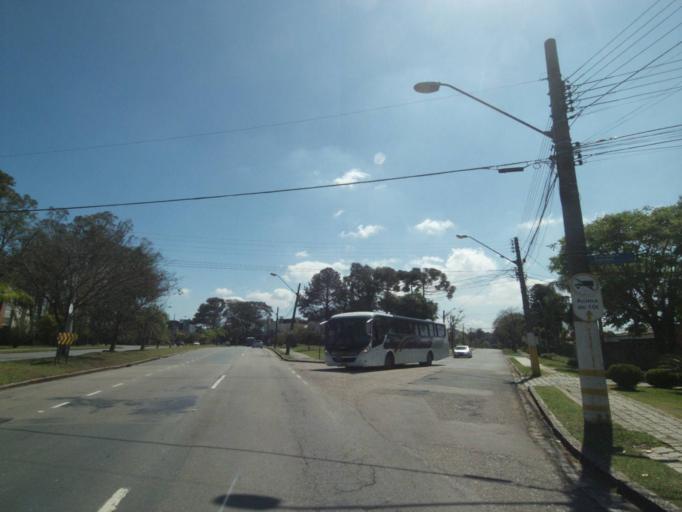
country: BR
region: Parana
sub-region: Curitiba
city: Curitiba
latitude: -25.4142
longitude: -49.2411
